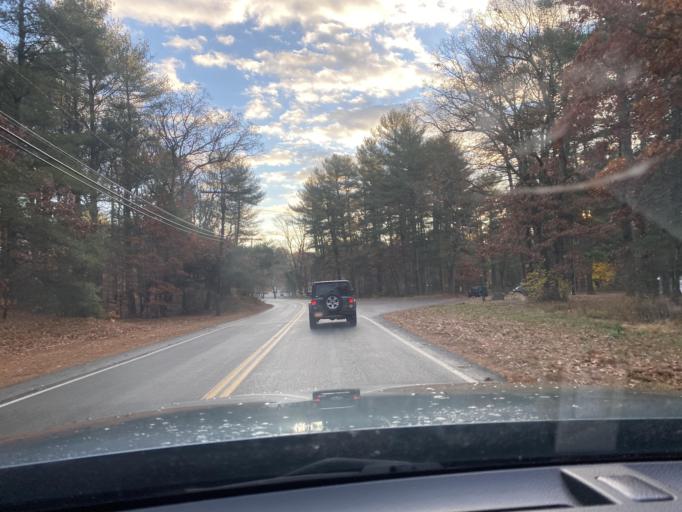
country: US
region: Massachusetts
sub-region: Norfolk County
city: Dover
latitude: 42.2483
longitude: -71.2701
